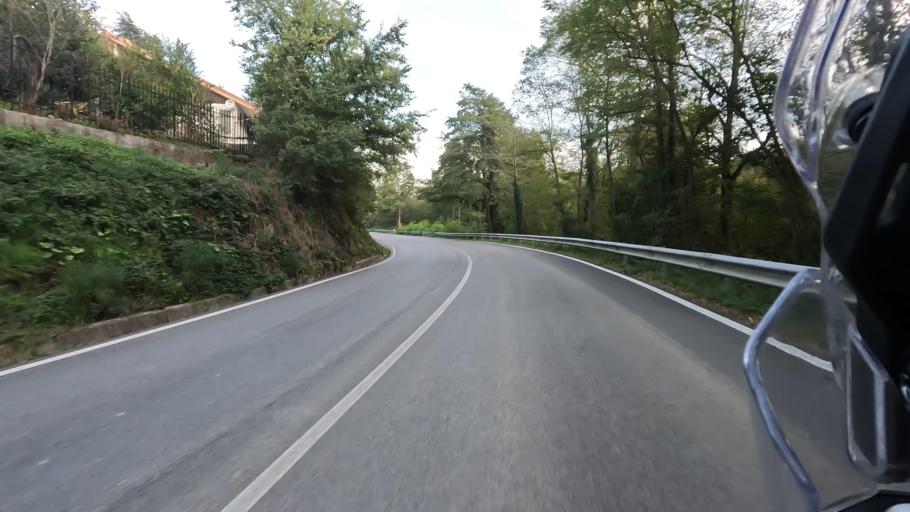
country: IT
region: Liguria
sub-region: Provincia di Savona
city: Osteria dei Cacciatori-Stella
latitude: 44.4327
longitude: 8.4554
